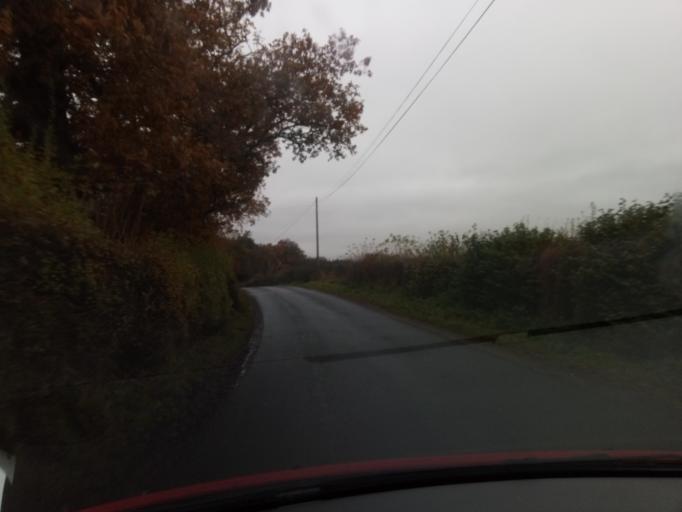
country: GB
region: Scotland
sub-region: The Scottish Borders
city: Newtown St Boswells
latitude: 55.5554
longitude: -2.6835
